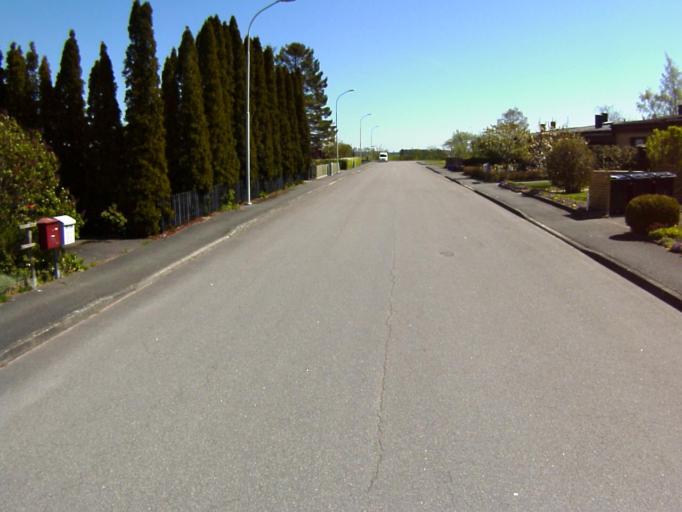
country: SE
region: Skane
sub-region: Kristianstads Kommun
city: Kristianstad
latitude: 56.0507
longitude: 14.2141
